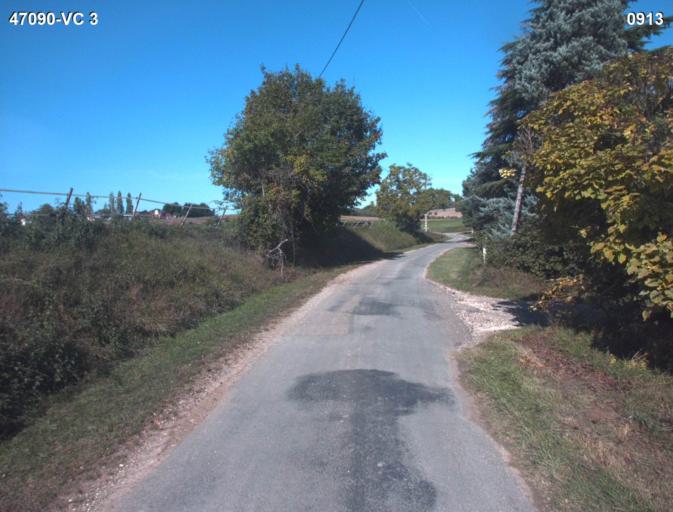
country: FR
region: Aquitaine
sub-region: Departement du Lot-et-Garonne
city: Nerac
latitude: 44.1714
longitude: 0.4093
